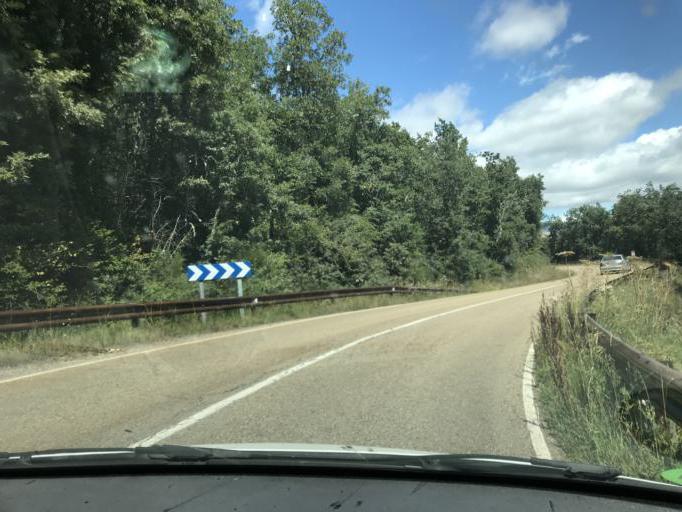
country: ES
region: Castille and Leon
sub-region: Provincia de Palencia
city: Cervera de Pisuerga
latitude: 42.9047
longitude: -4.4945
